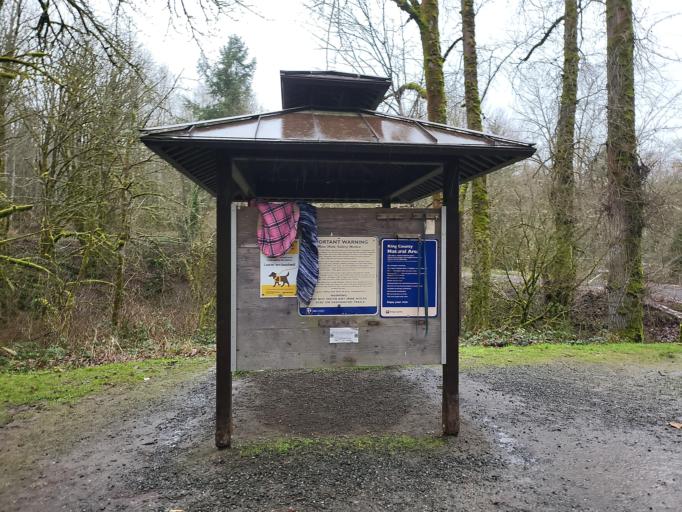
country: US
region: Washington
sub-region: King County
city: Newcastle
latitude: 47.5345
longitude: -122.1286
